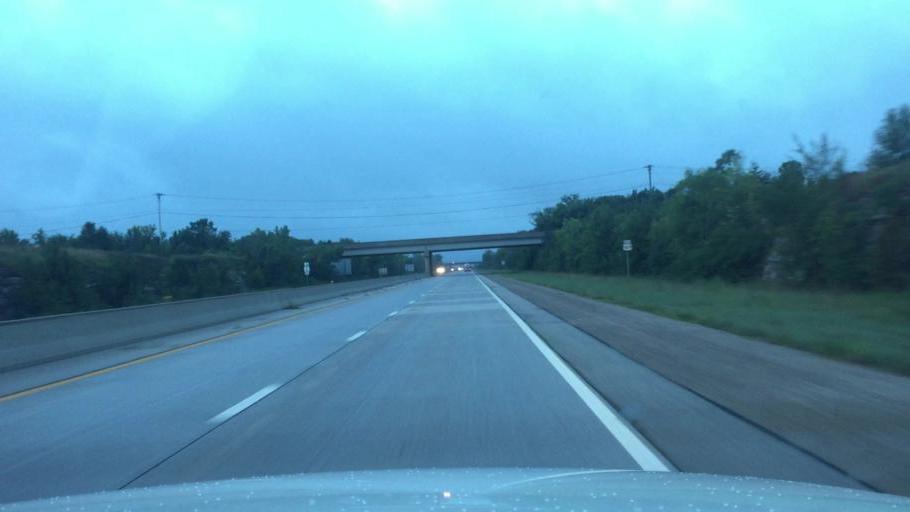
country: US
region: Kansas
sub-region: Neosho County
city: Chanute
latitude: 37.6837
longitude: -95.4796
